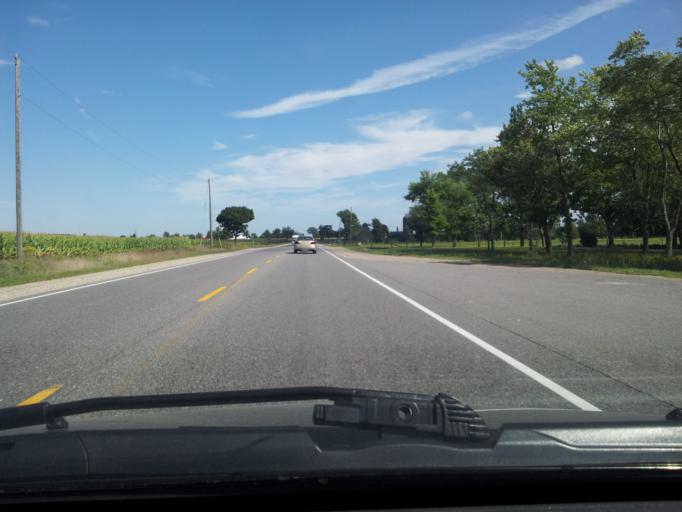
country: CA
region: Ontario
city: Stratford
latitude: 43.3690
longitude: -80.7713
